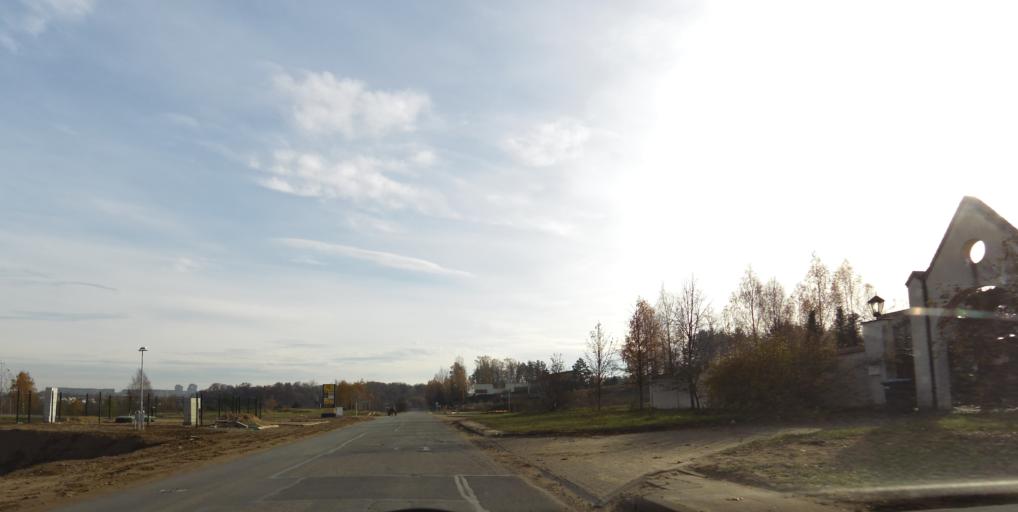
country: LT
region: Vilnius County
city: Pilaite
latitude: 54.7233
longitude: 25.1896
